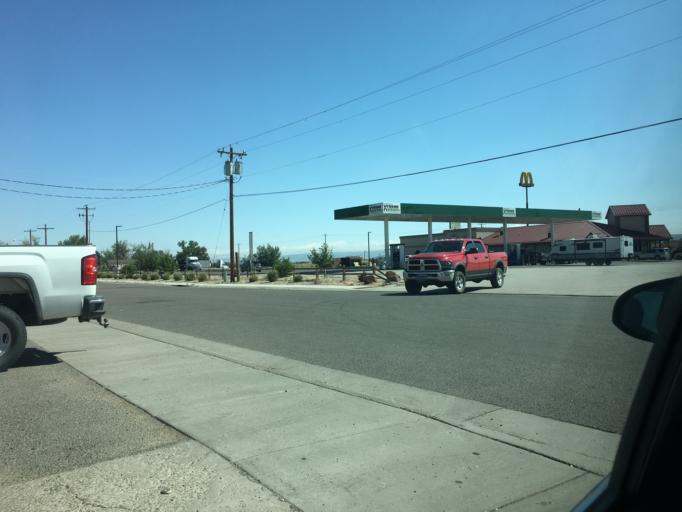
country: US
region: Wyoming
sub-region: Albany County
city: Laramie
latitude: 41.3092
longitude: -105.6173
